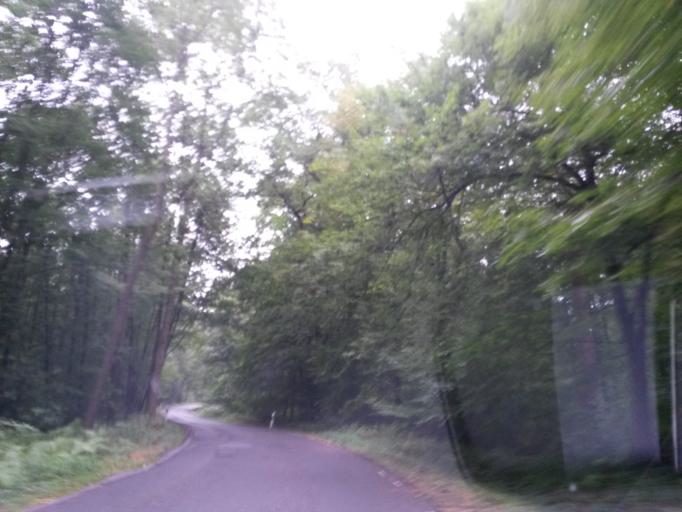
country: DE
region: North Rhine-Westphalia
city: Wiehl
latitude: 50.9653
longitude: 7.5616
